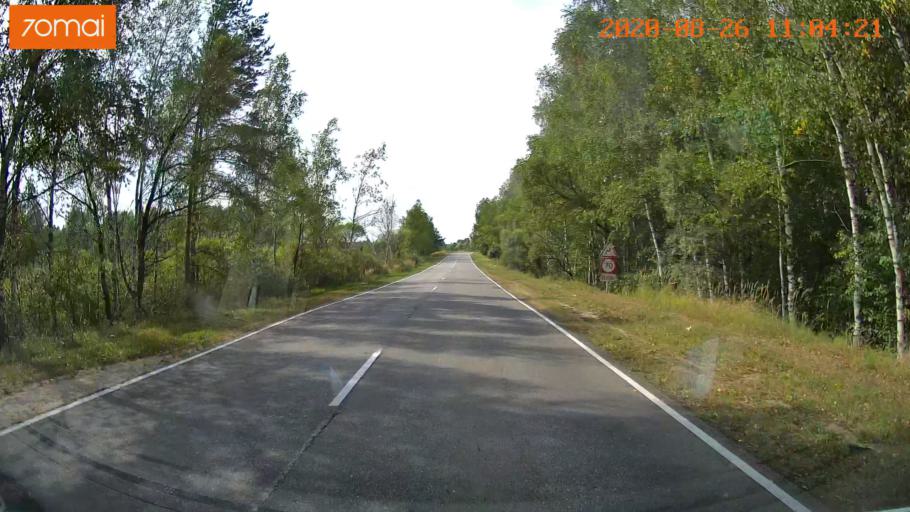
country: RU
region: Rjazan
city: Izhevskoye
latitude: 54.5308
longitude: 41.1969
